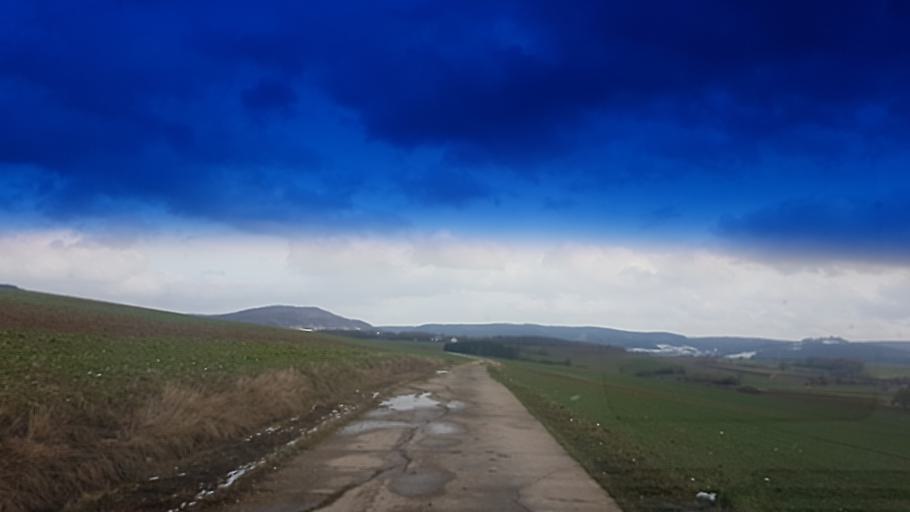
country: DE
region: Bavaria
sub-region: Upper Franconia
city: Schesslitz
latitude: 50.0038
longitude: 11.0052
